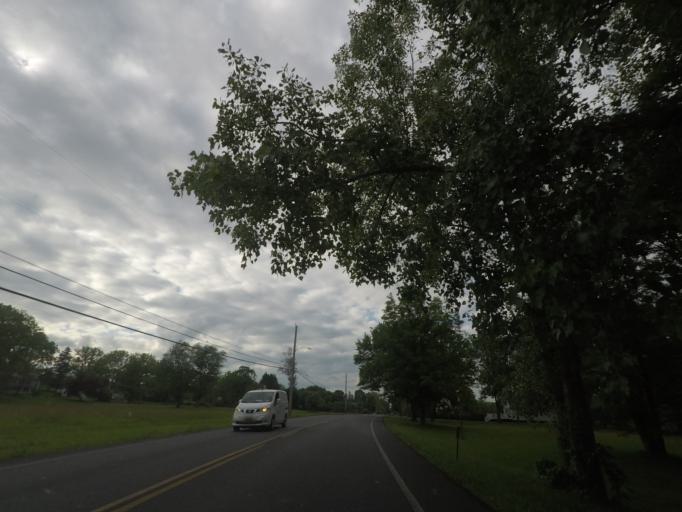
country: US
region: New York
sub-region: Orange County
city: Orange Lake
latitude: 41.5860
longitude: -74.1180
